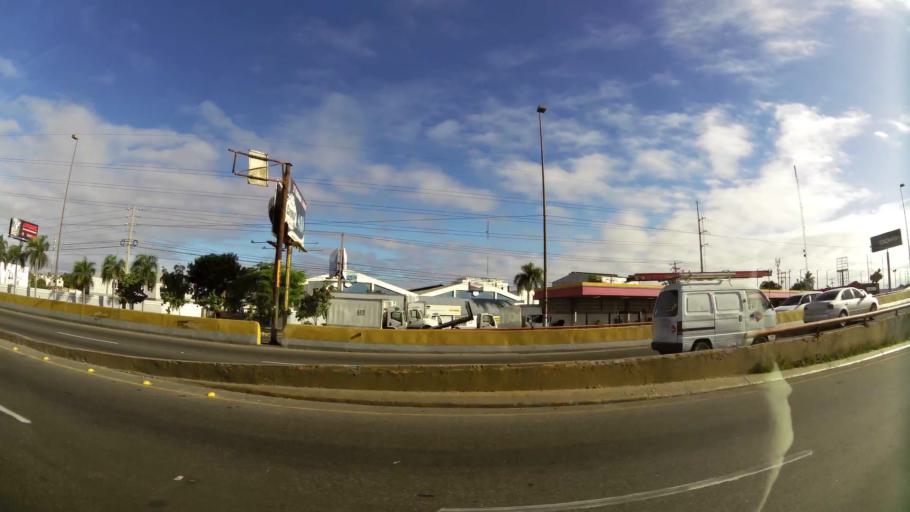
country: DO
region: Nacional
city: La Julia
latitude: 18.4829
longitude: -69.9331
